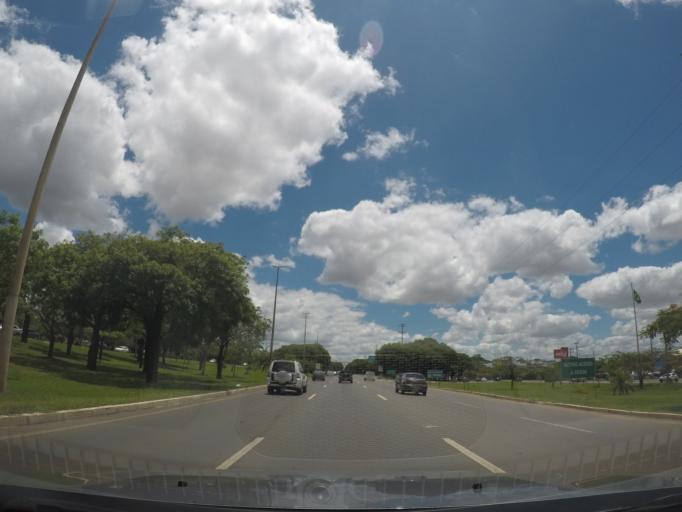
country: BR
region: Federal District
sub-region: Brasilia
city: Brasilia
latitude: -15.7932
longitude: -47.9441
